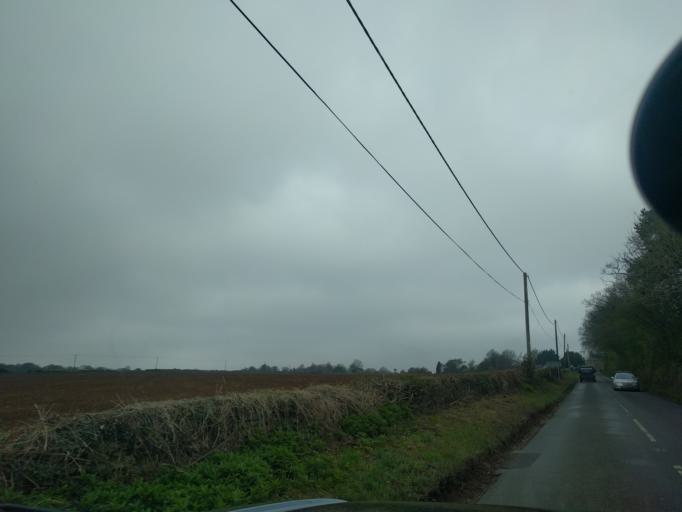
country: GB
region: England
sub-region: Wiltshire
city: Box
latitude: 51.4035
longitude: -2.2406
